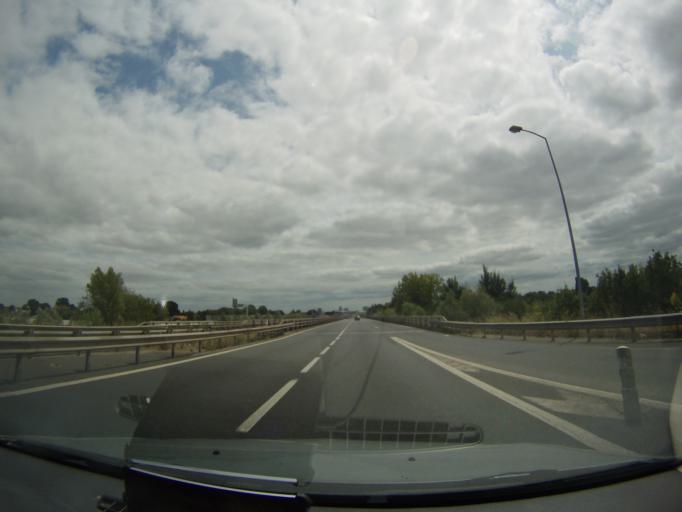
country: FR
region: Pays de la Loire
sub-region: Departement de la Loire-Atlantique
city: Sainte-Luce-sur-Loire
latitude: 47.2359
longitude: -1.4794
